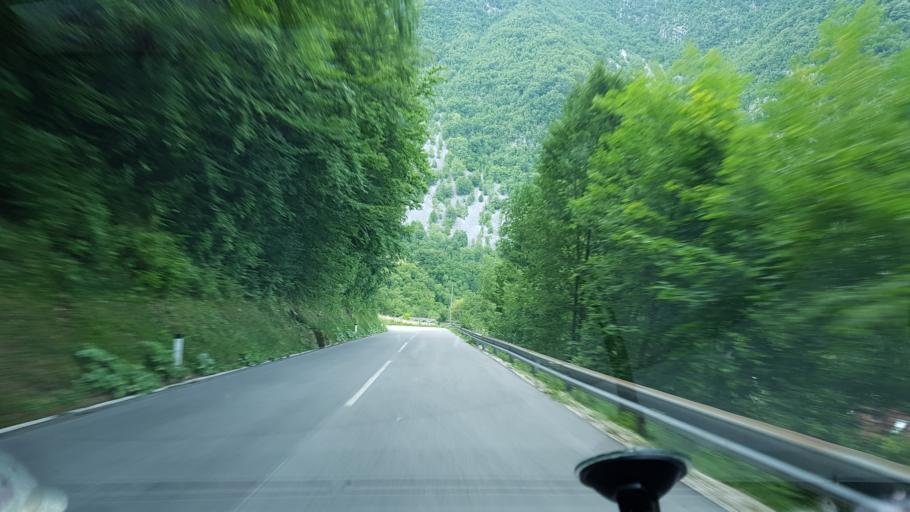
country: SI
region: Bovec
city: Bovec
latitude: 46.3082
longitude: 13.4704
